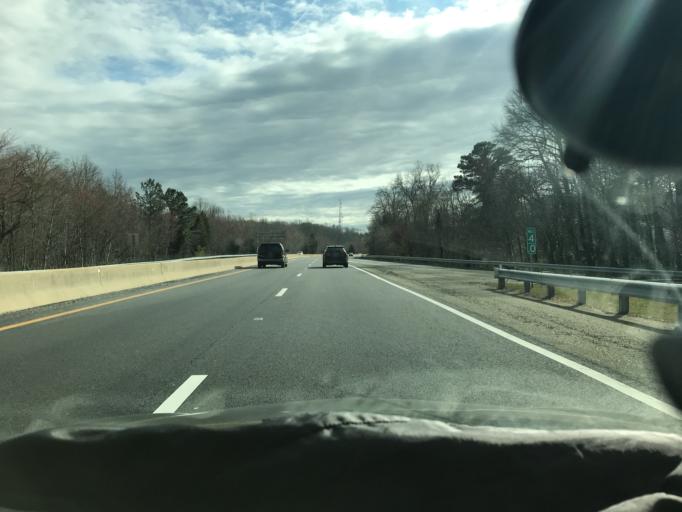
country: US
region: Virginia
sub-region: Chesterfield County
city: Bon Air
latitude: 37.5165
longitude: -77.5355
